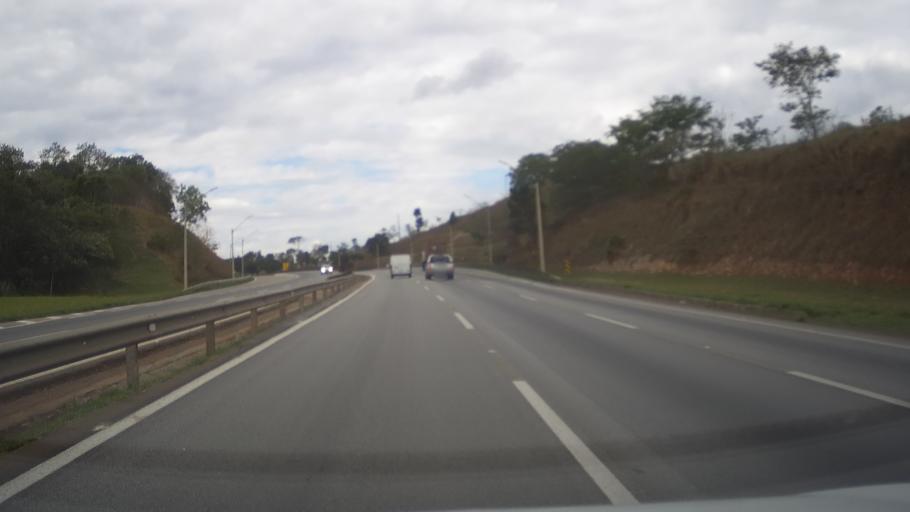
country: BR
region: Minas Gerais
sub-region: Itauna
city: Itauna
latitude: -20.3466
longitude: -44.4421
